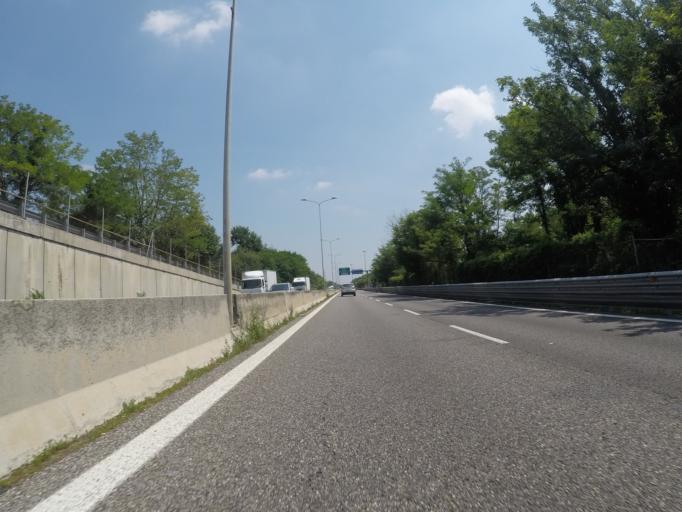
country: IT
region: Lombardy
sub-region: Provincia di Varese
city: Gallarate
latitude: 45.6403
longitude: 8.8106
